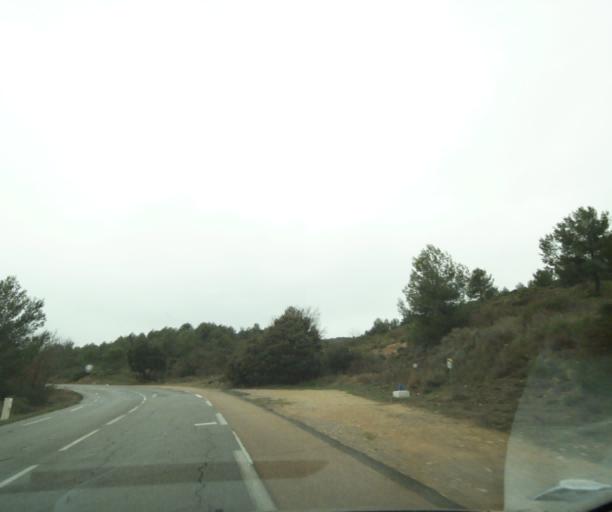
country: FR
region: Provence-Alpes-Cote d'Azur
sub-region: Departement des Bouches-du-Rhone
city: Le Puy-Sainte-Reparade
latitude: 43.6601
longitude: 5.3948
